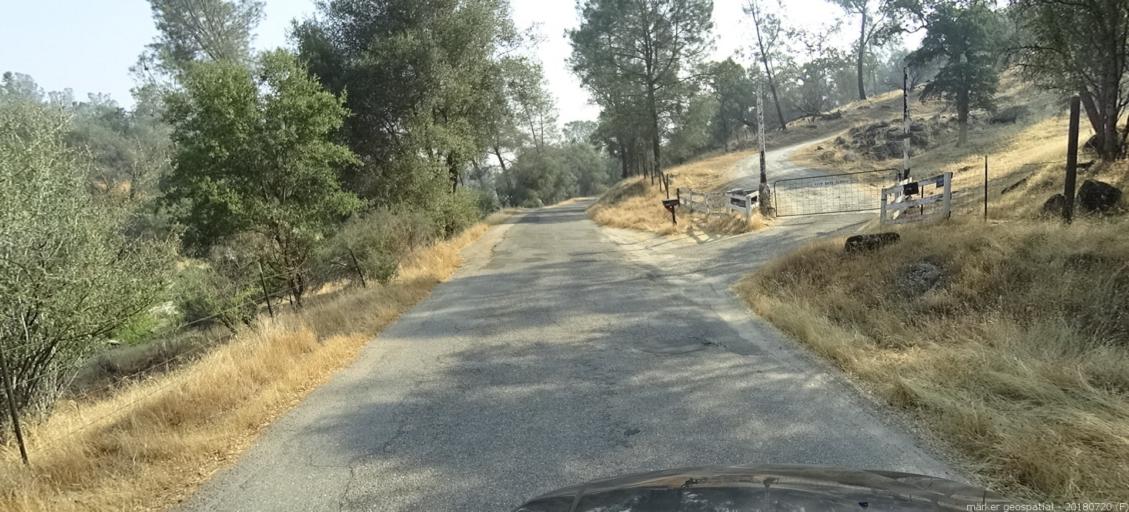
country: US
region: California
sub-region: Madera County
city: Yosemite Lakes
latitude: 37.2842
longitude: -119.8709
